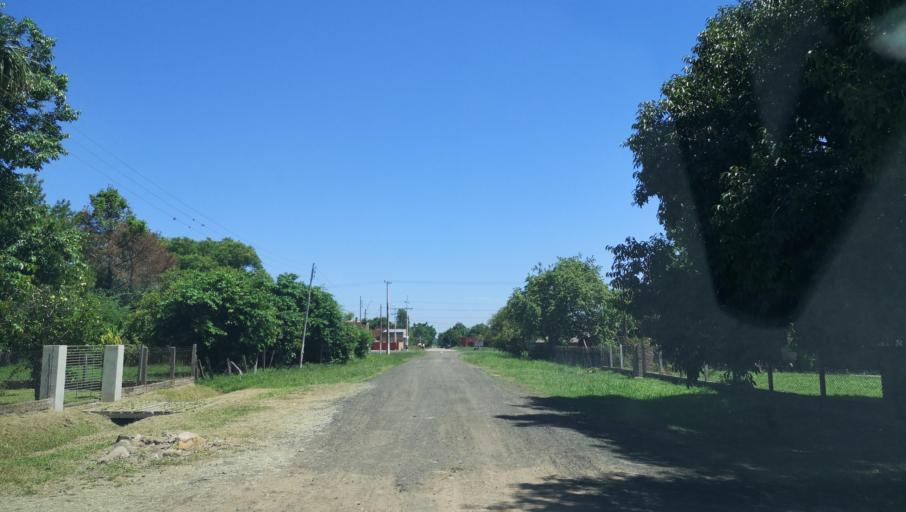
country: PY
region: Caaguazu
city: Carayao
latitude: -25.1992
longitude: -56.3958
